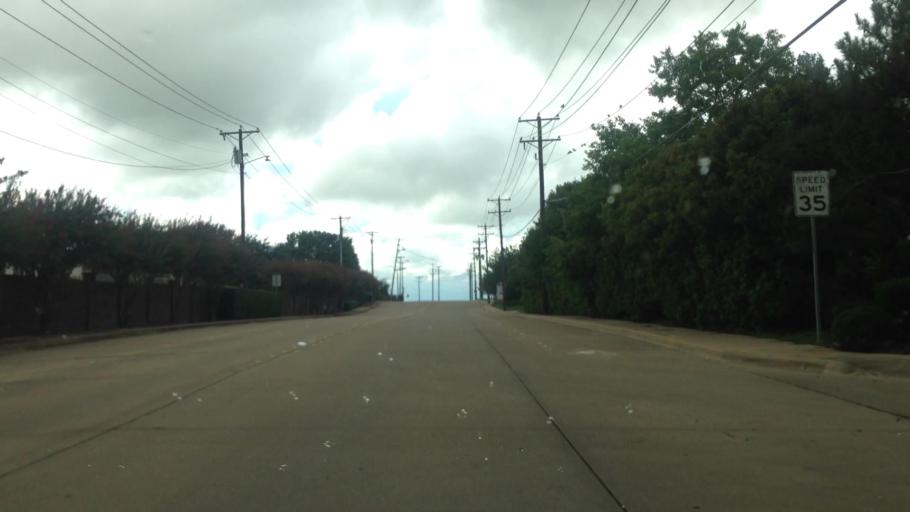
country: US
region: Texas
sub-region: Tarrant County
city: Crowley
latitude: 32.6286
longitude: -97.4038
